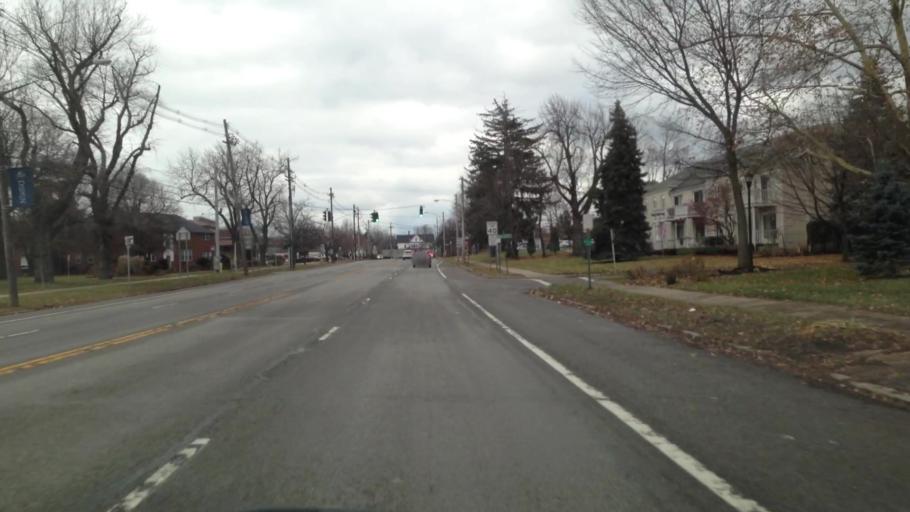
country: US
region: New York
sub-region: Erie County
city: Eggertsville
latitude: 42.9636
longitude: -78.7877
